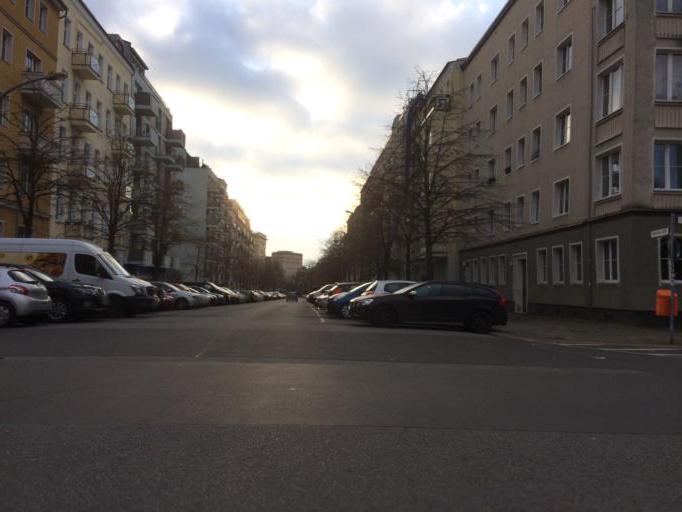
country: DE
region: Berlin
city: Friedrichshain Bezirk
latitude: 52.5196
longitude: 13.4478
